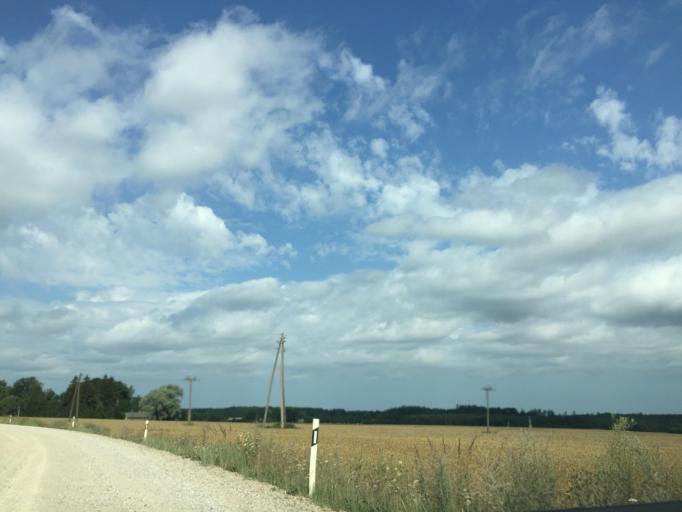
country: LV
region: Kandava
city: Kandava
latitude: 56.9969
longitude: 22.8879
